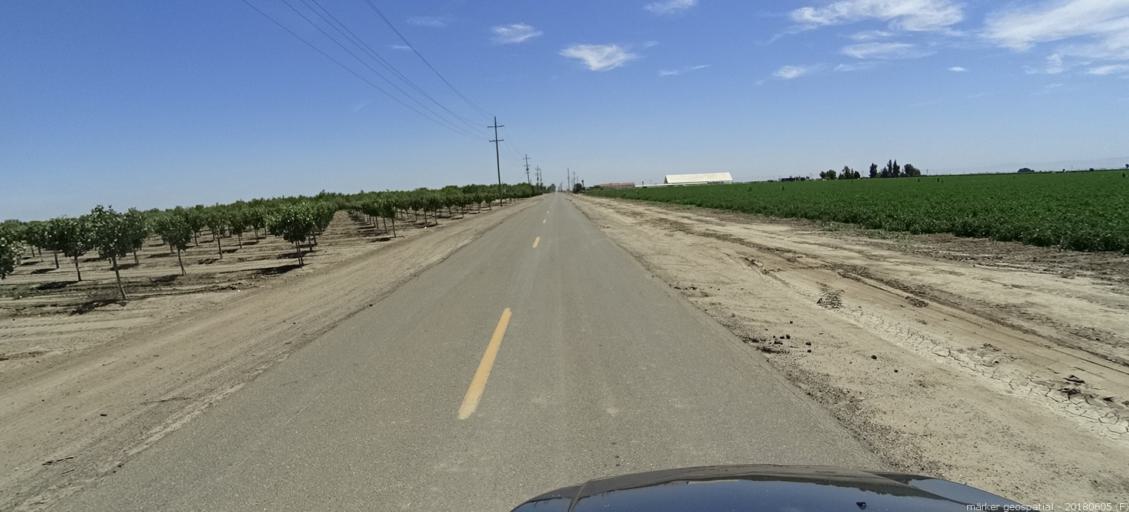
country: US
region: California
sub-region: Merced County
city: Dos Palos
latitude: 37.0890
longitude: -120.4734
